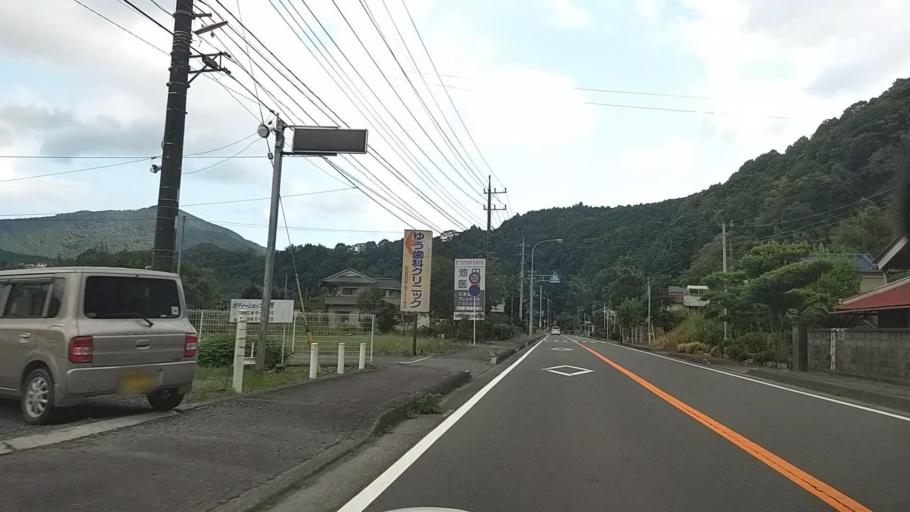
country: JP
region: Shizuoka
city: Fujinomiya
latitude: 35.2291
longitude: 138.5080
